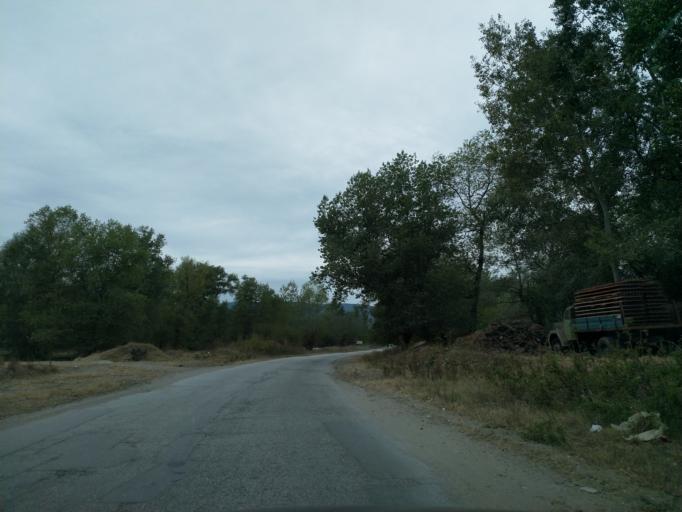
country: RS
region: Central Serbia
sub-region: Pomoravski Okrug
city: Paracin
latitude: 43.8265
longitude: 21.3515
